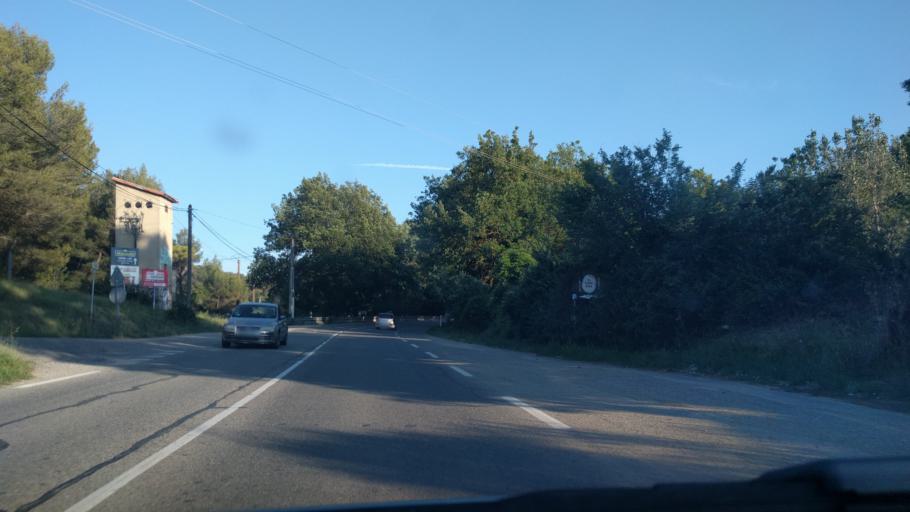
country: FR
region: Provence-Alpes-Cote d'Azur
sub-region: Departement des Bouches-du-Rhone
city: Venelles
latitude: 43.6316
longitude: 5.4876
